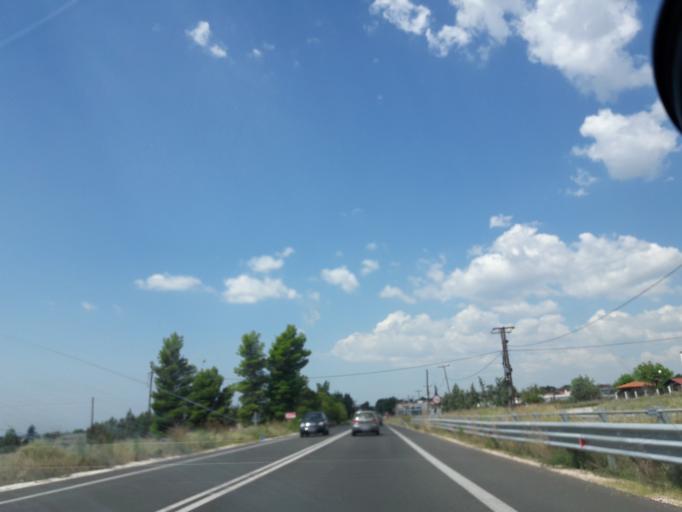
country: GR
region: Central Macedonia
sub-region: Nomos Thessalonikis
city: Agia Paraskevi
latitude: 40.5201
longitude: 23.0595
